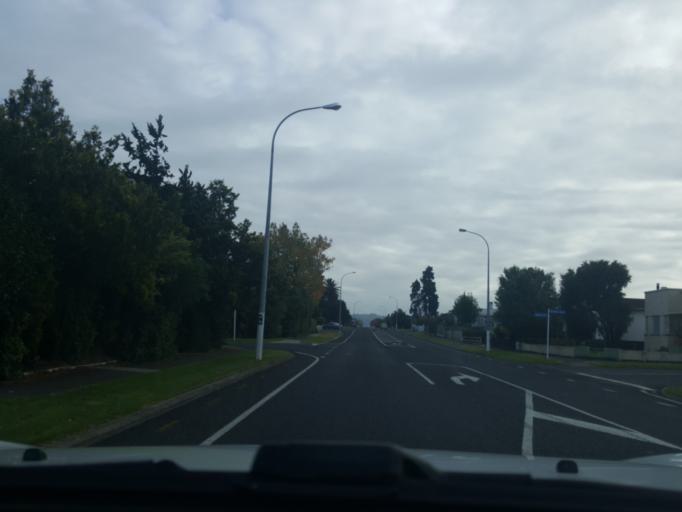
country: NZ
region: Waikato
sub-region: Hauraki District
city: Paeroa
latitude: -37.5323
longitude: 175.7068
